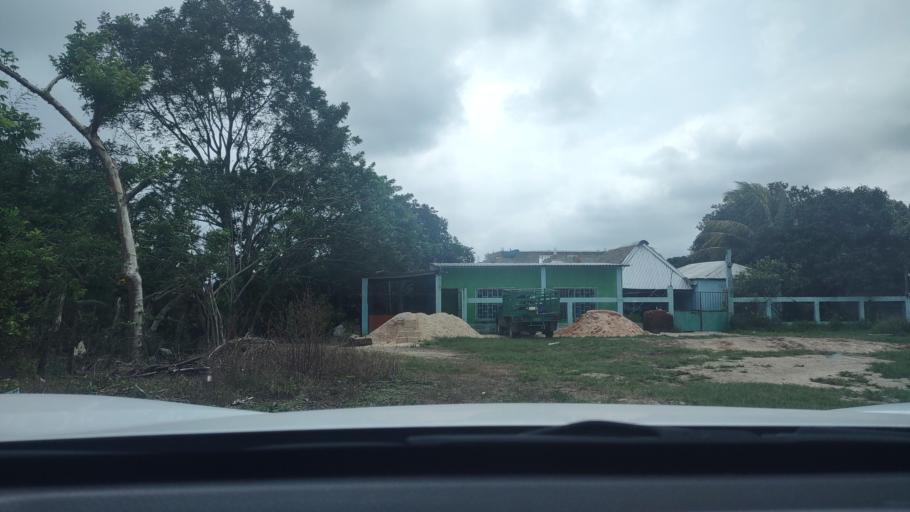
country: MX
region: Veracruz
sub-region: Moloacan
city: Cuichapa
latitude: 17.8981
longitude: -94.2997
